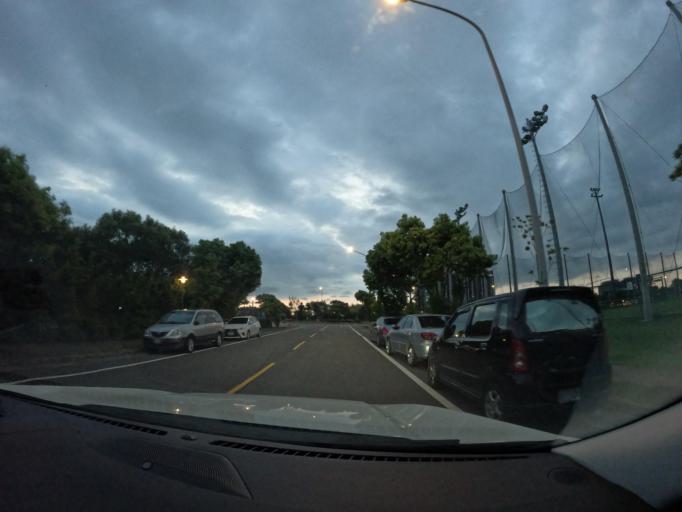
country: TW
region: Taiwan
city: Taoyuan City
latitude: 25.0130
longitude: 121.2093
